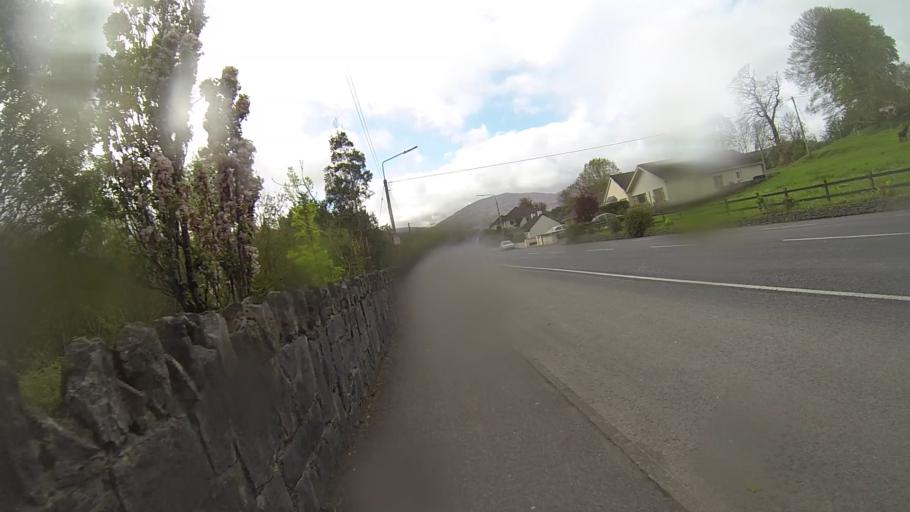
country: IE
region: Munster
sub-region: Ciarrai
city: Kenmare
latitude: 51.8831
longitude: -9.5855
